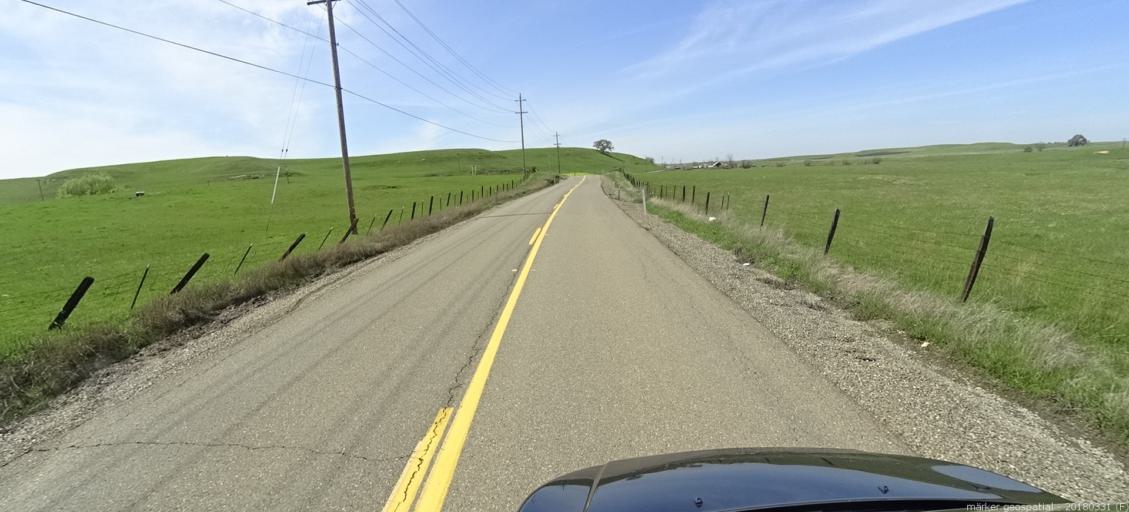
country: US
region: California
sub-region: Sacramento County
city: Rancho Murieta
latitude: 38.5169
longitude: -121.1106
